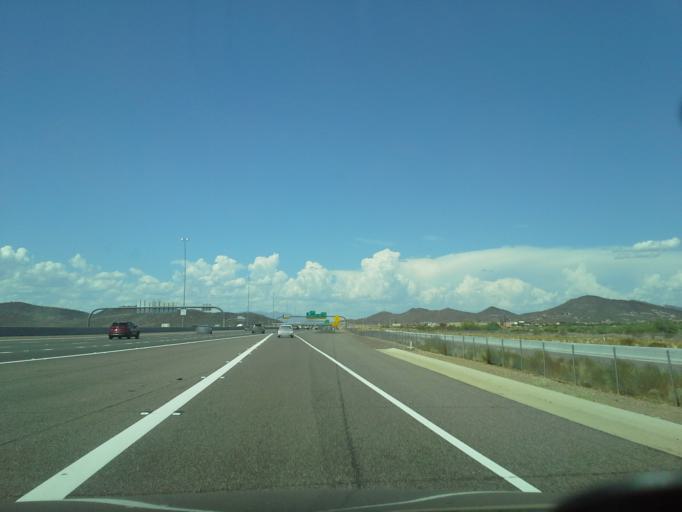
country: US
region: Arizona
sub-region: Maricopa County
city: Anthem
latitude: 33.7880
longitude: -112.1329
